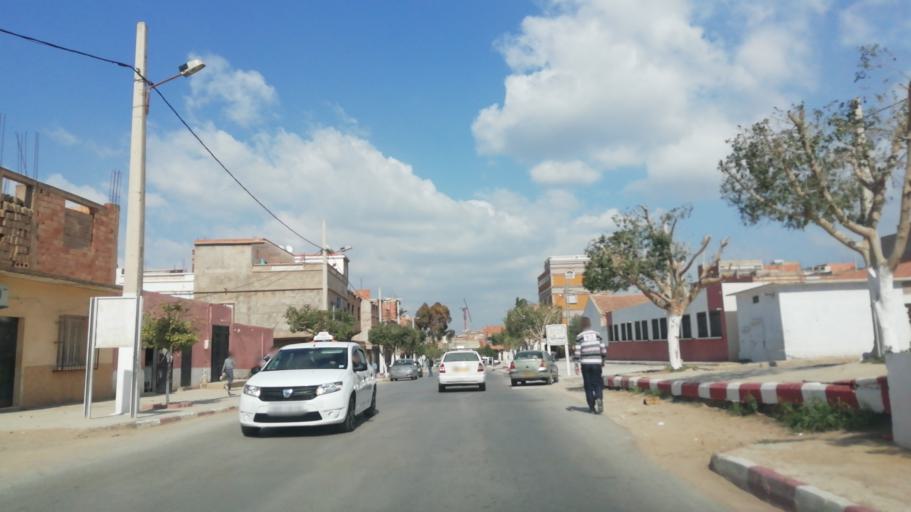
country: DZ
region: Mascara
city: Mascara
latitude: 35.5726
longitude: 0.0691
